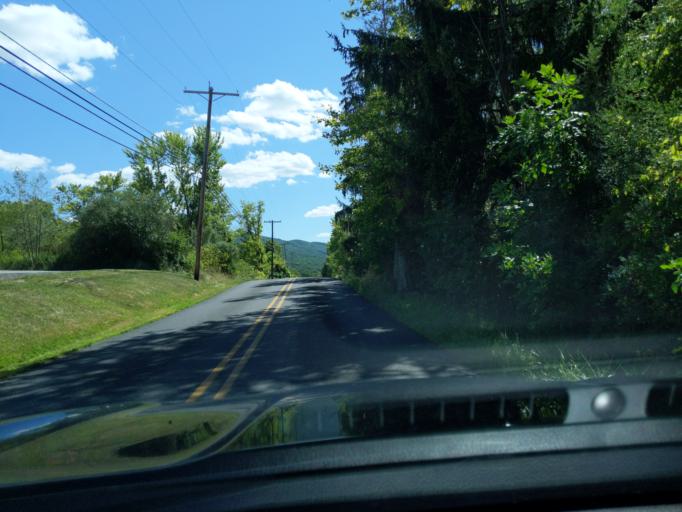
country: US
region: Pennsylvania
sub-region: Blair County
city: Williamsburg
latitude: 40.4813
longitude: -78.2713
